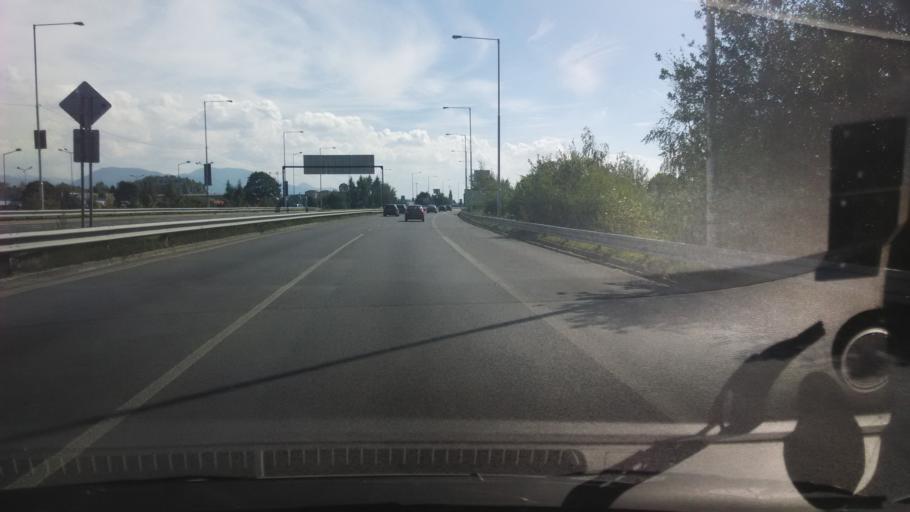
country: SK
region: Zilinsky
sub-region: Okres Martin
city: Martin
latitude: 49.0857
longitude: 18.9219
